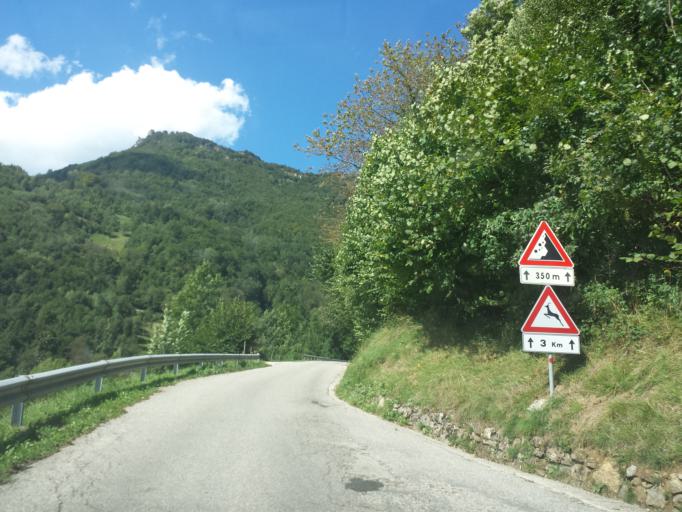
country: IT
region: Veneto
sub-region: Provincia di Vicenza
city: Recoaro Terme
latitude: 45.7170
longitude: 11.1979
